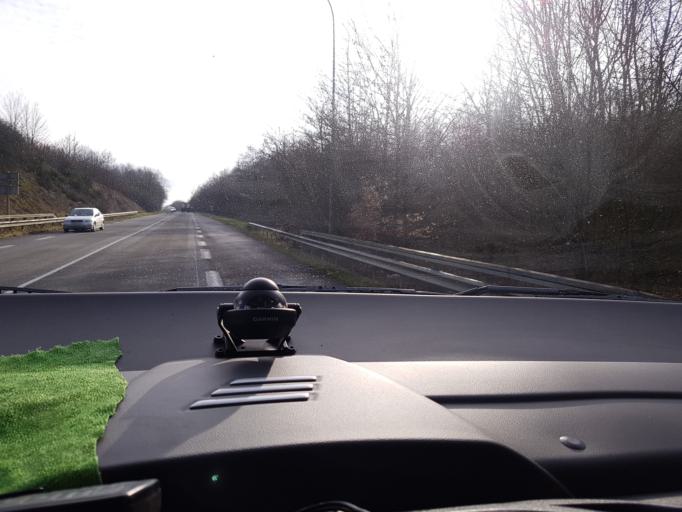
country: FR
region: Nord-Pas-de-Calais
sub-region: Departement du Nord
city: Fourmies
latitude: 50.0148
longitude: 4.0294
